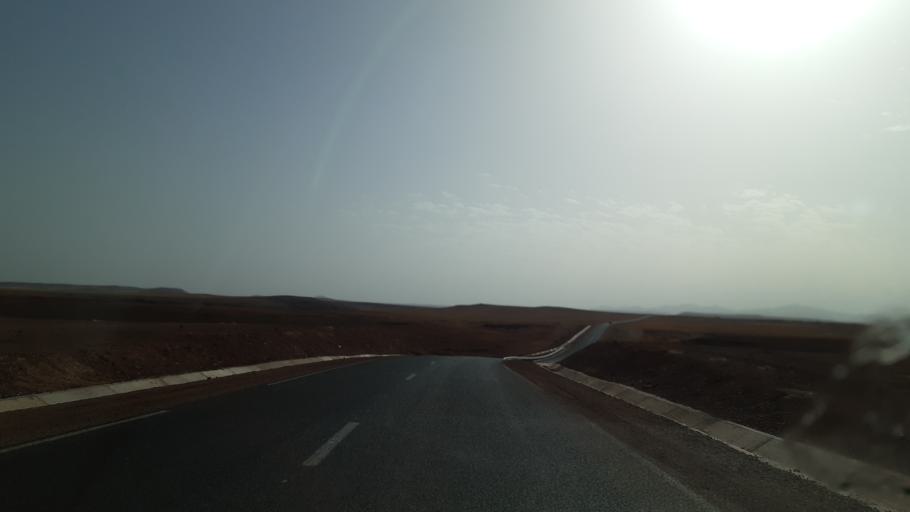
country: MA
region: Meknes-Tafilalet
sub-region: Khenifra
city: Itzer
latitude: 32.8649
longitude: -4.8845
